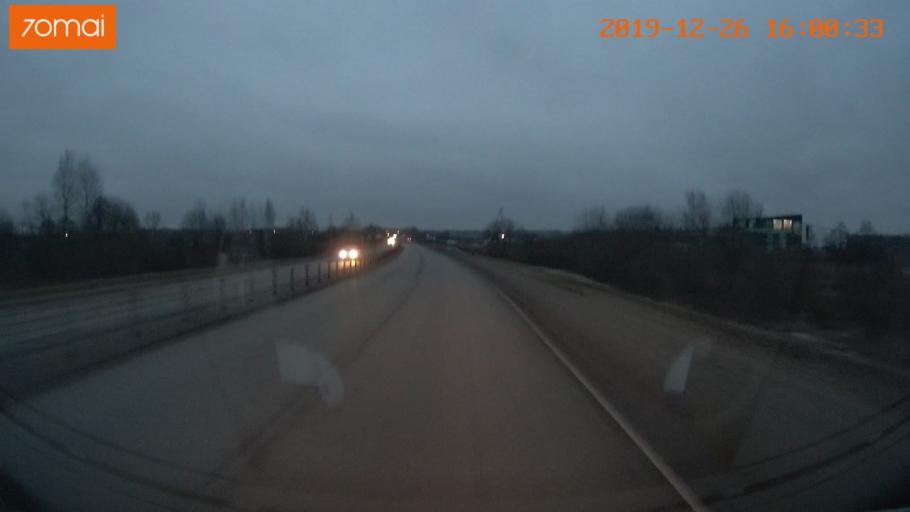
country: RU
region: Jaroslavl
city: Rybinsk
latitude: 58.0233
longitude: 38.8037
